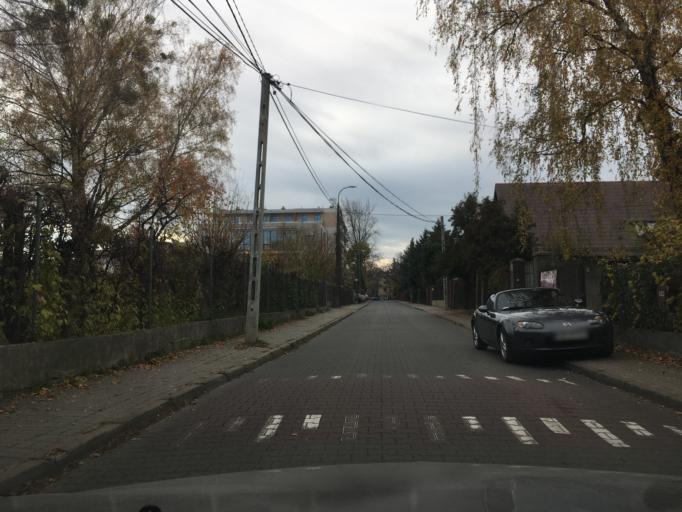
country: PL
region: Masovian Voivodeship
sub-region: Powiat piaseczynski
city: Piaseczno
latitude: 52.0699
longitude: 21.0228
